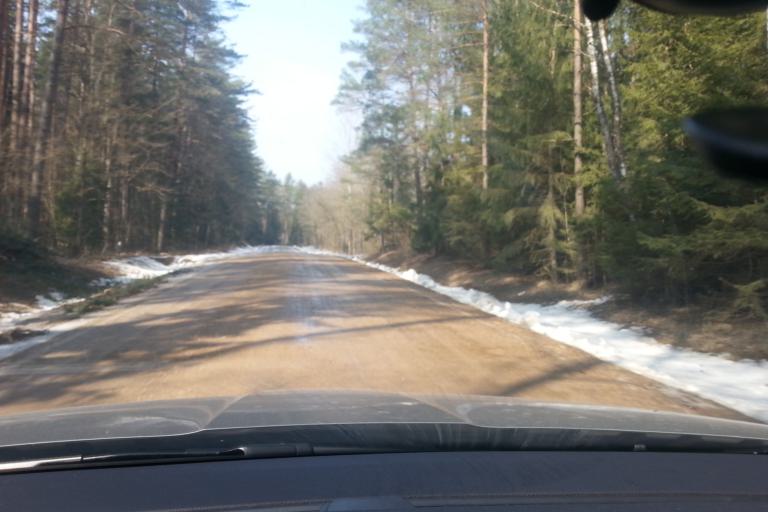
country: LT
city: Trakai
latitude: 54.5672
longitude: 24.9707
